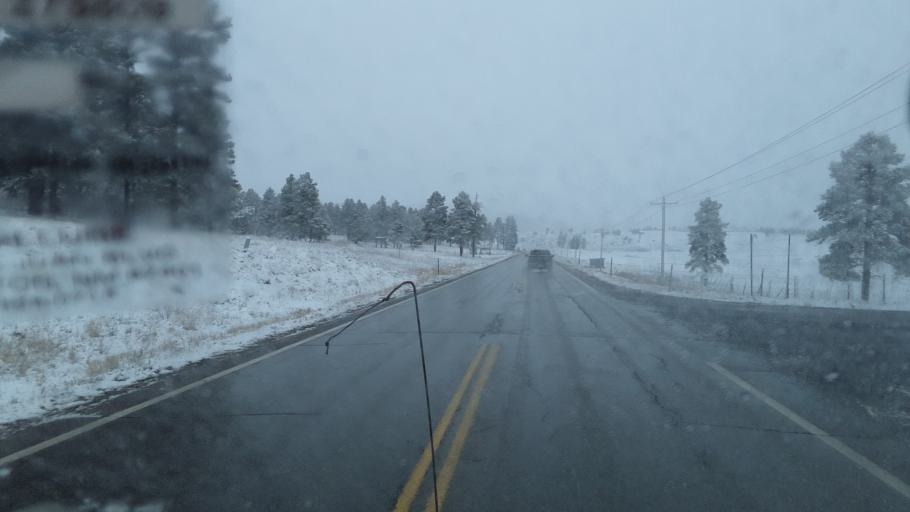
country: US
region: Colorado
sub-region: Archuleta County
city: Pagosa Springs
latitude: 37.2349
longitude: -106.9853
